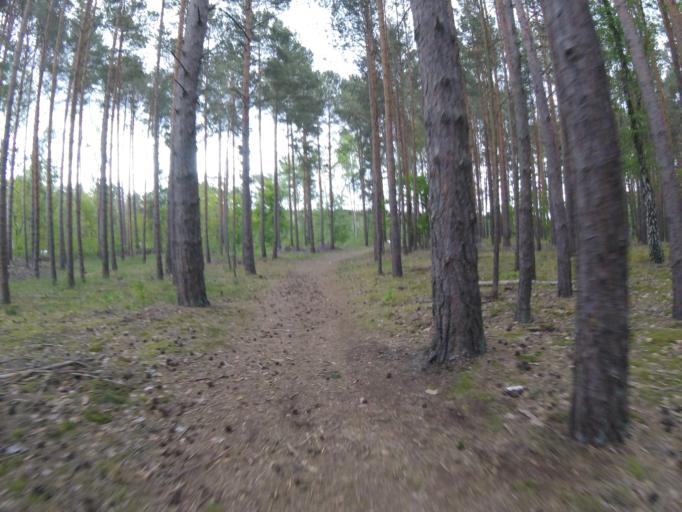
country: DE
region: Brandenburg
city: Bestensee
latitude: 52.2546
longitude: 13.6671
